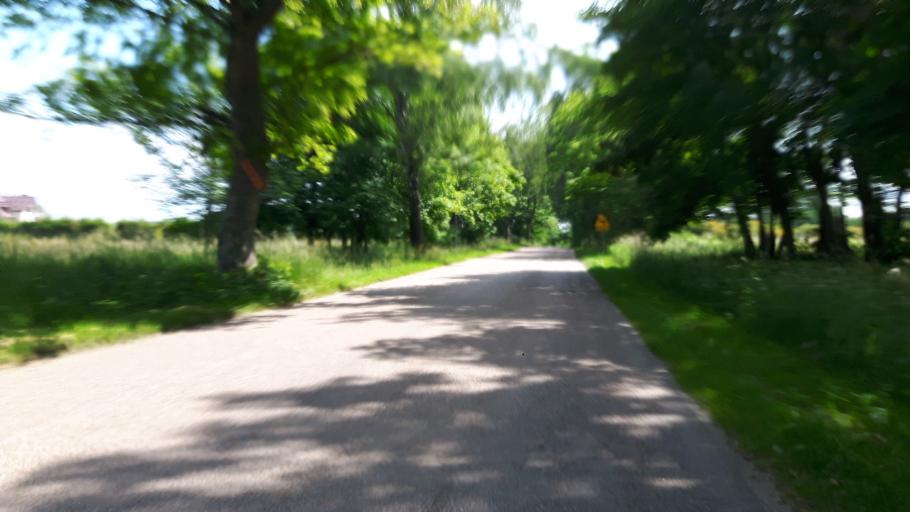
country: PL
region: Pomeranian Voivodeship
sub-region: Powiat wejherowski
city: Choczewo
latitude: 54.7573
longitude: 17.7794
